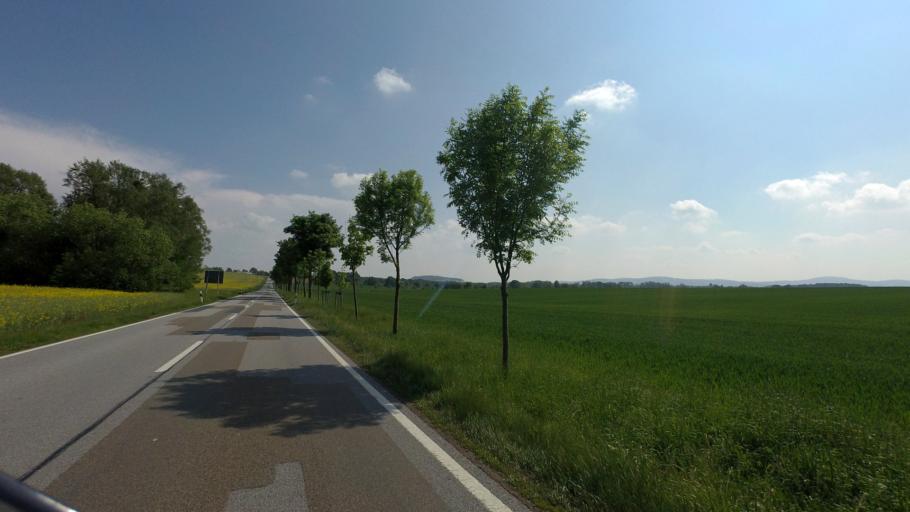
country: DE
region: Saxony
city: Weissenberg
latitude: 51.1859
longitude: 14.6426
